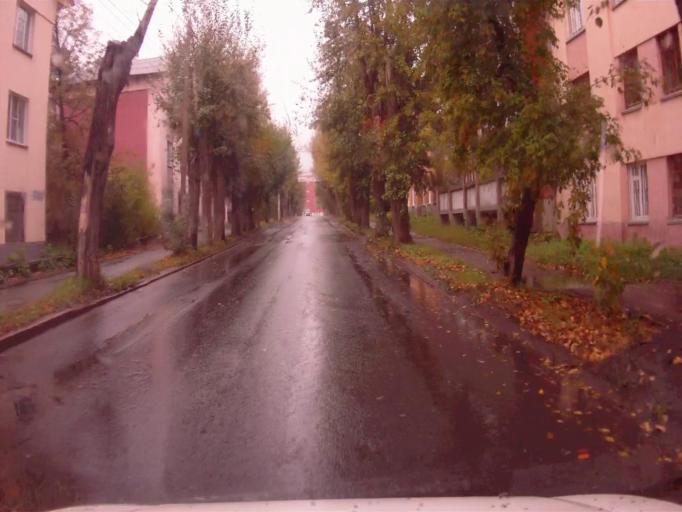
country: RU
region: Chelyabinsk
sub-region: Gorod Chelyabinsk
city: Chelyabinsk
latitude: 55.1967
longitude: 61.4085
